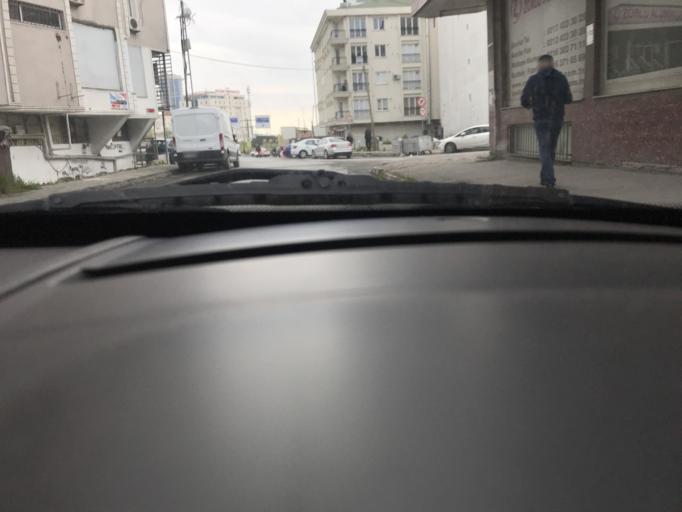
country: TR
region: Istanbul
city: Yakuplu
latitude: 41.0018
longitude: 28.6989
